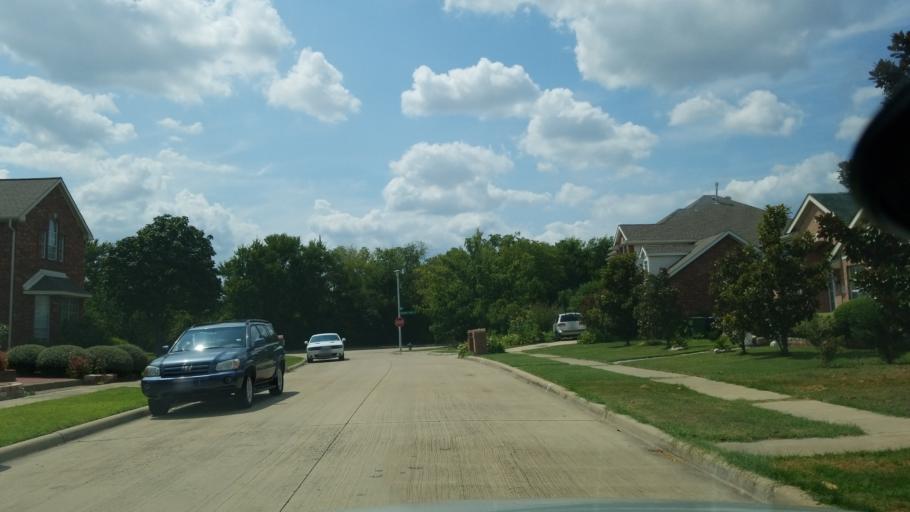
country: US
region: Texas
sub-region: Dallas County
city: Garland
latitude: 32.9280
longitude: -96.6631
